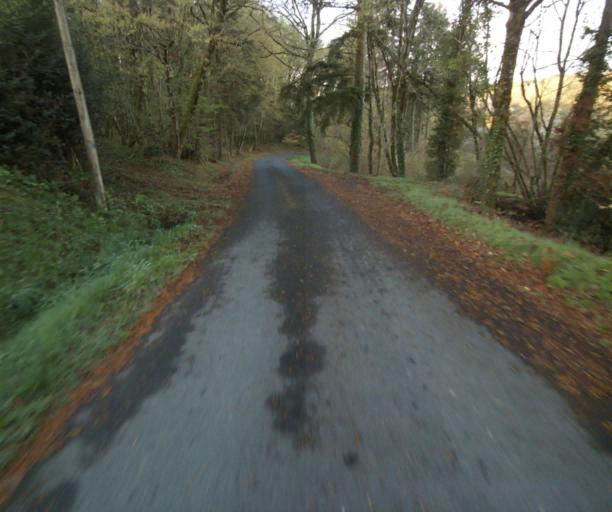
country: FR
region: Limousin
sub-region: Departement de la Correze
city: Naves
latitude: 45.3203
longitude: 1.8334
